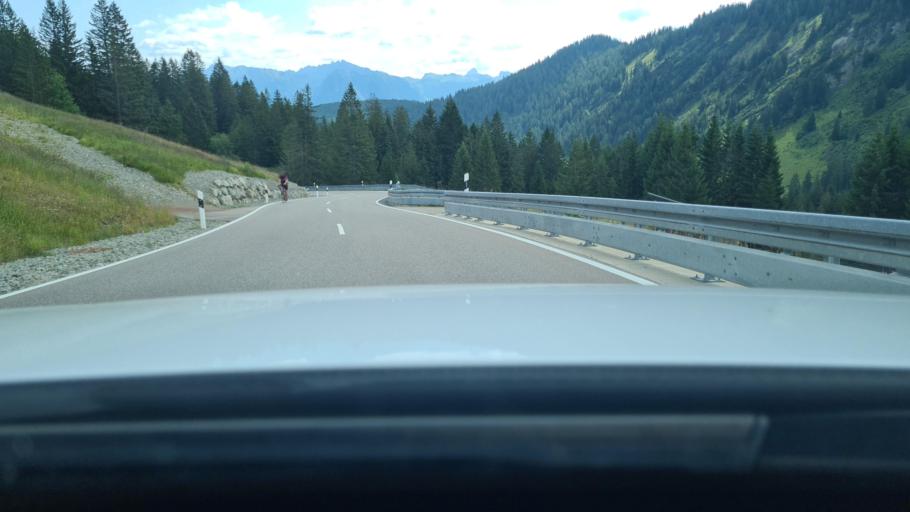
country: DE
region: Bavaria
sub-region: Swabia
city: Obermaiselstein
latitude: 47.4348
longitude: 10.1805
